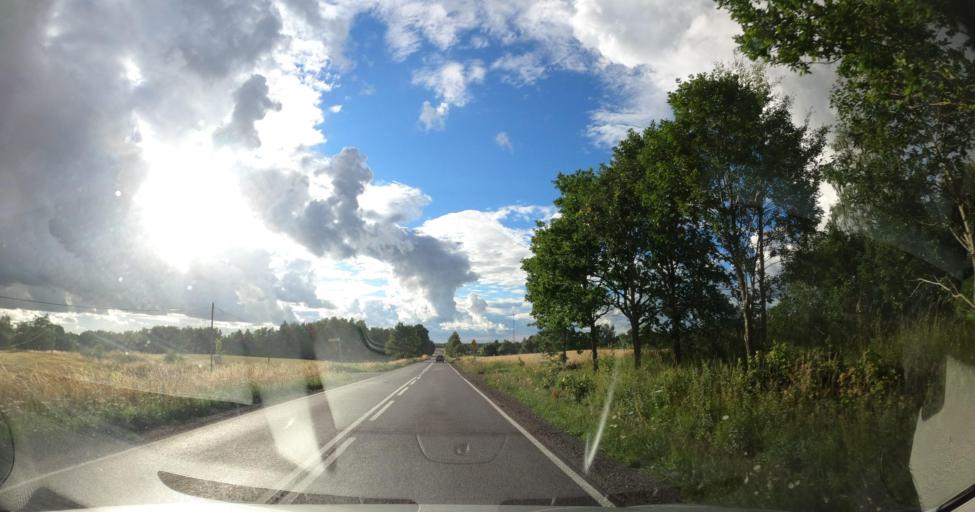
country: PL
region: Pomeranian Voivodeship
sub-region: Powiat bytowski
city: Czarna Dabrowka
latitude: 54.3493
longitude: 17.5812
